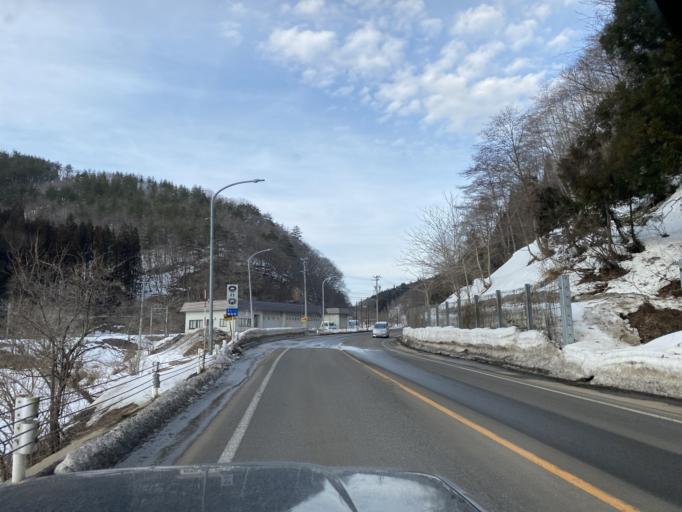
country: JP
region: Nagano
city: Omachi
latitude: 36.5805
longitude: 137.8392
